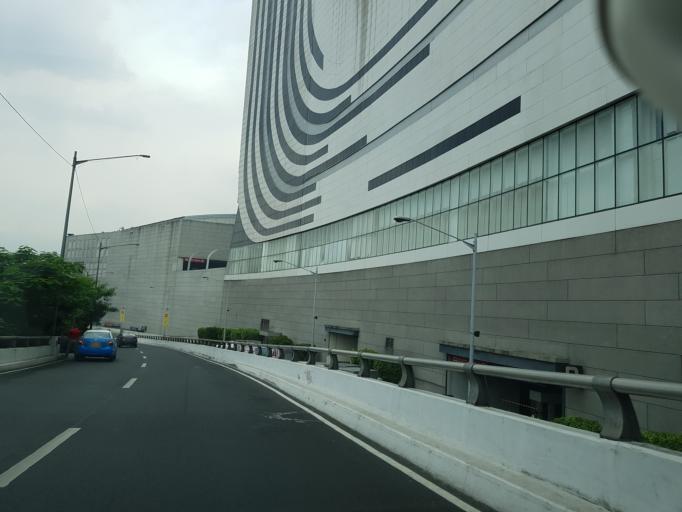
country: PH
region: Calabarzon
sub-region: Province of Rizal
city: Pateros
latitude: 14.5457
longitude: 121.0542
